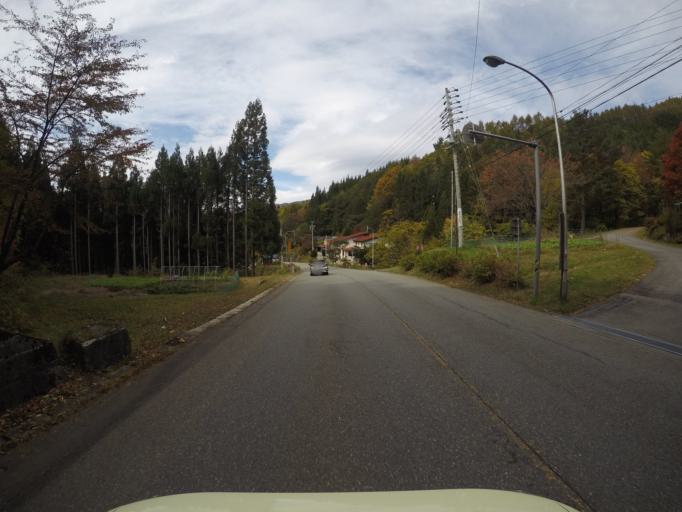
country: JP
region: Gifu
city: Takayama
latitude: 36.1800
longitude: 137.4787
